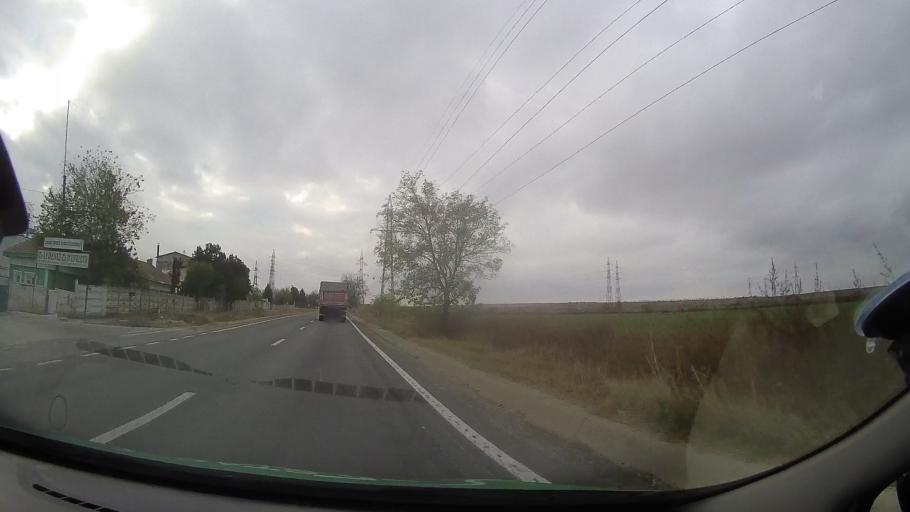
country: RO
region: Constanta
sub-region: Municipiul Medgidia
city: Medgidia
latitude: 44.2679
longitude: 28.2724
